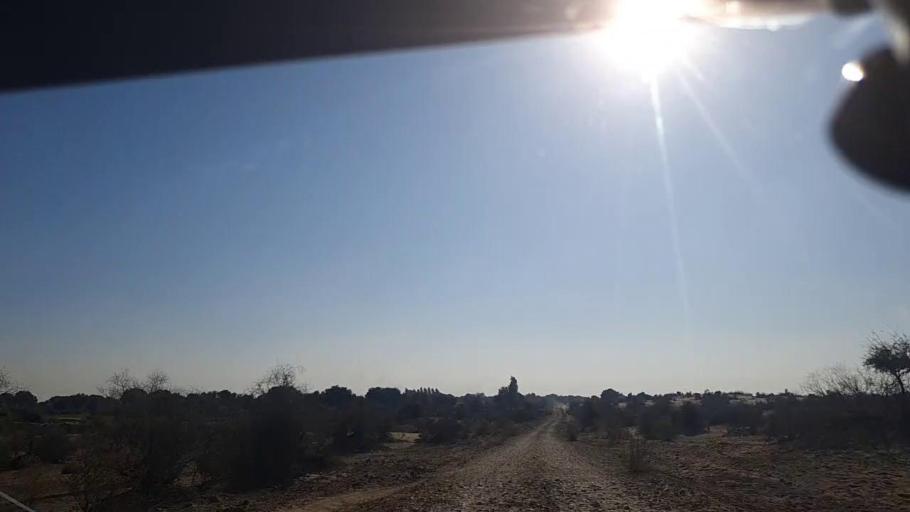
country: PK
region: Sindh
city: Khanpur
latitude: 27.6399
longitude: 69.4049
